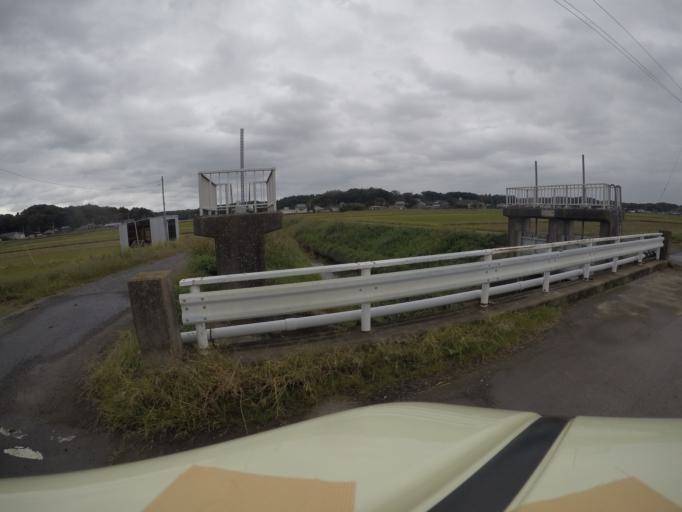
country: JP
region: Ibaraki
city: Itako
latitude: 36.0433
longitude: 140.4490
